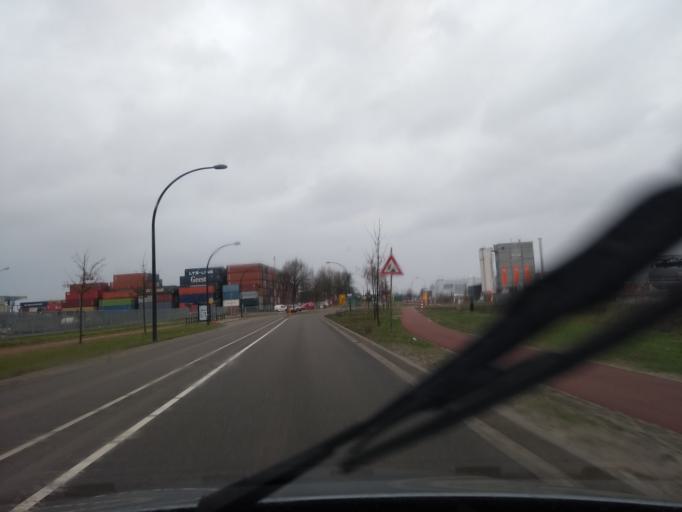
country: NL
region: Overijssel
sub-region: Gemeente Hengelo
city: Hengelo
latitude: 52.2444
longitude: 6.7885
